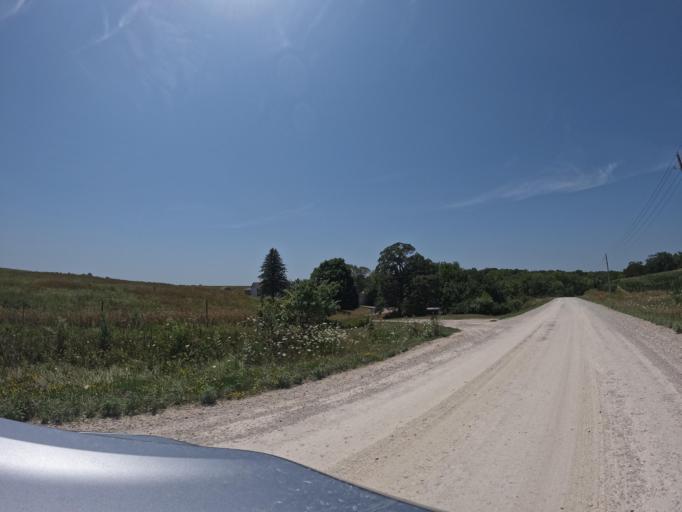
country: US
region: Iowa
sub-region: Henry County
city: Mount Pleasant
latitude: 40.9270
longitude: -91.6273
